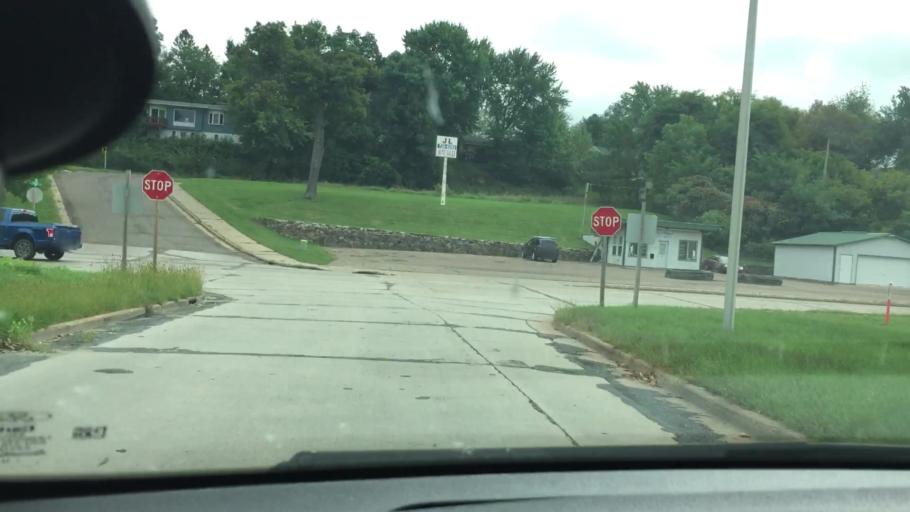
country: US
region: Wisconsin
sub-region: Chippewa County
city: Chippewa Falls
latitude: 44.9278
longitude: -91.3854
